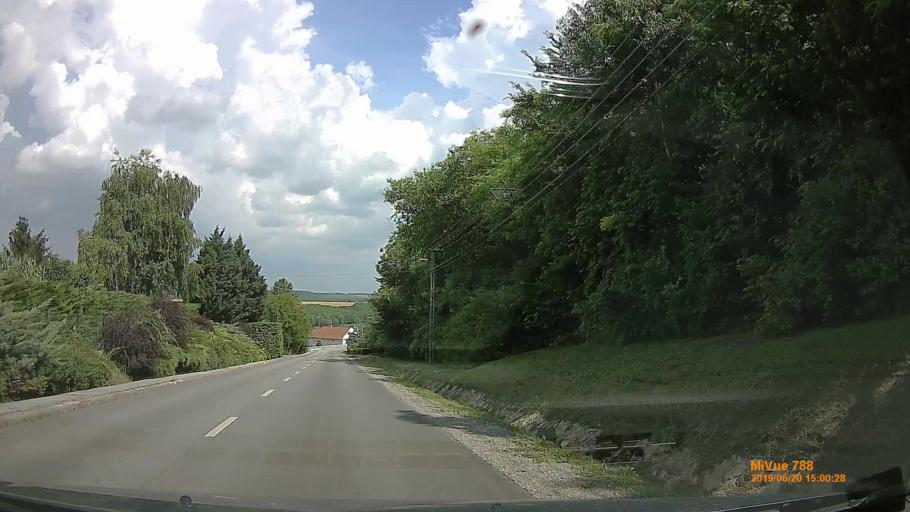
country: HU
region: Baranya
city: Kozarmisleny
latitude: 45.9853
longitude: 18.2580
